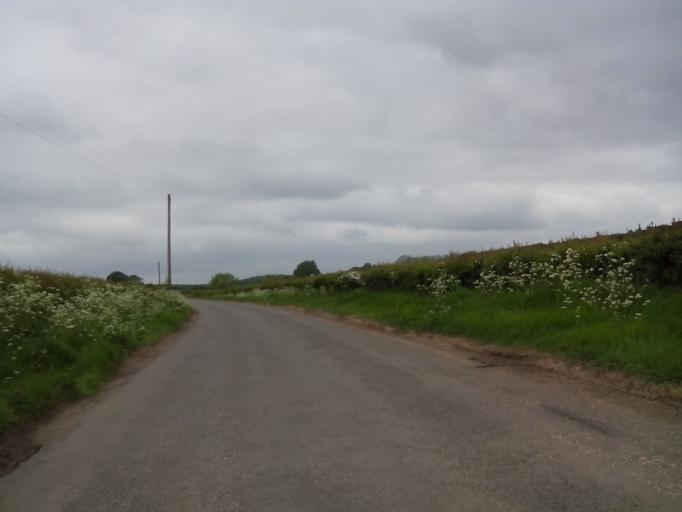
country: GB
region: England
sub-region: Northamptonshire
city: Oundle
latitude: 52.5165
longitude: -0.5145
